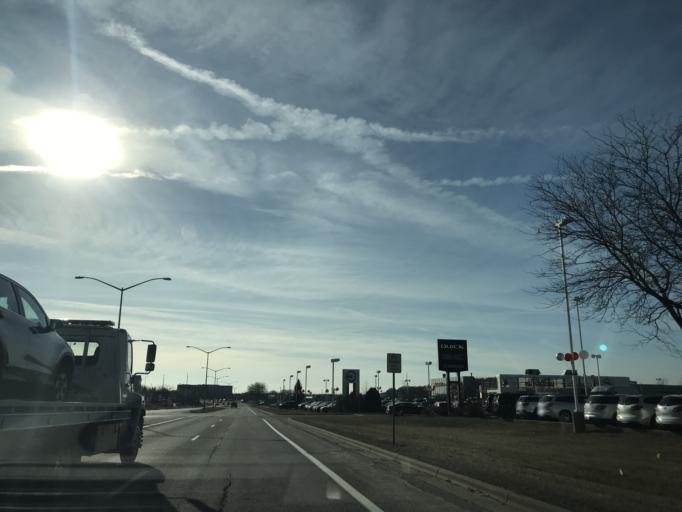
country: US
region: Wisconsin
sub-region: Dane County
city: Sun Prairie
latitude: 43.1411
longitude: -89.2865
